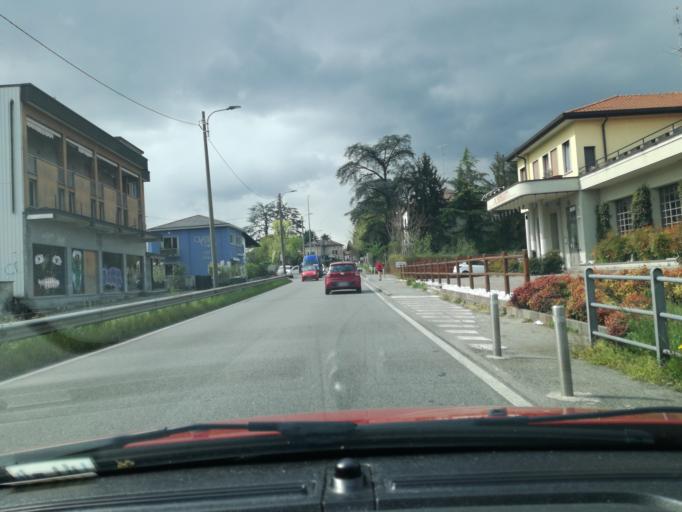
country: IT
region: Lombardy
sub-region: Provincia di Monza e Brianza
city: Costa Lambro
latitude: 45.6788
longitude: 9.2453
